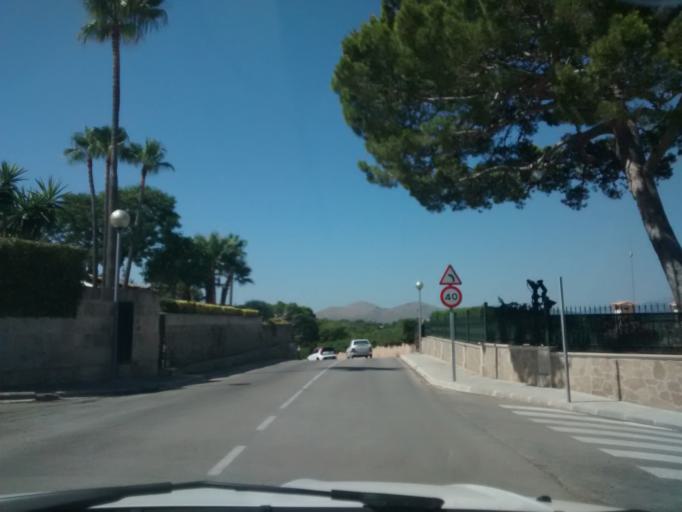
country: ES
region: Balearic Islands
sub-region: Illes Balears
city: Port d'Alcudia
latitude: 39.8683
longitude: 3.1503
